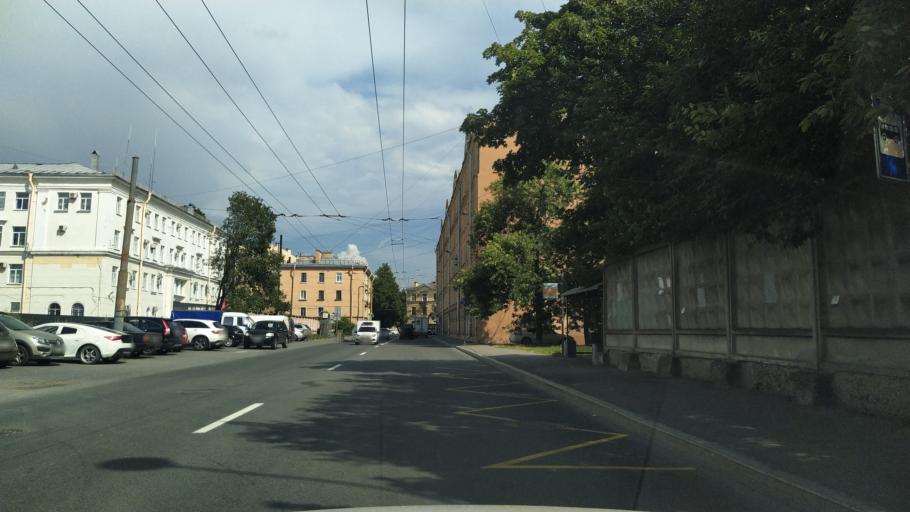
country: RU
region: Leningrad
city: Finlyandskiy
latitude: 59.9660
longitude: 30.3796
